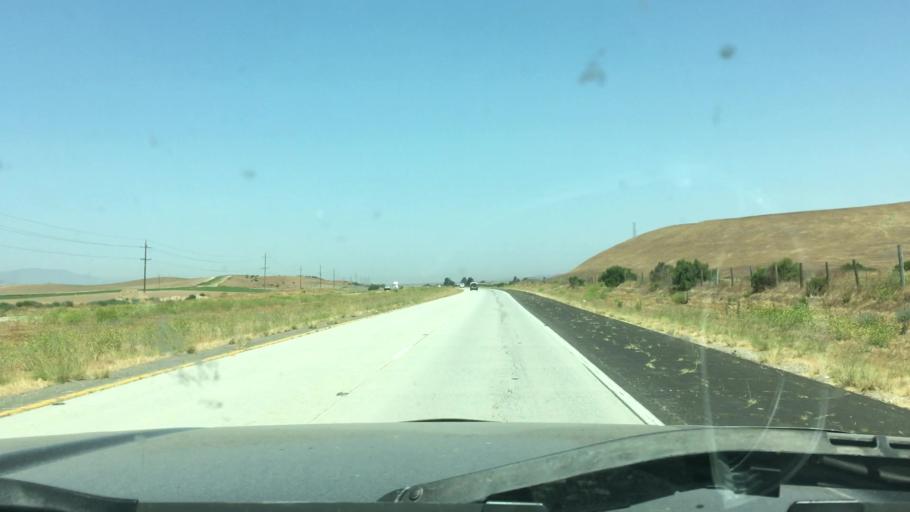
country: US
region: California
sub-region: Monterey County
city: King City
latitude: 36.1549
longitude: -121.0459
